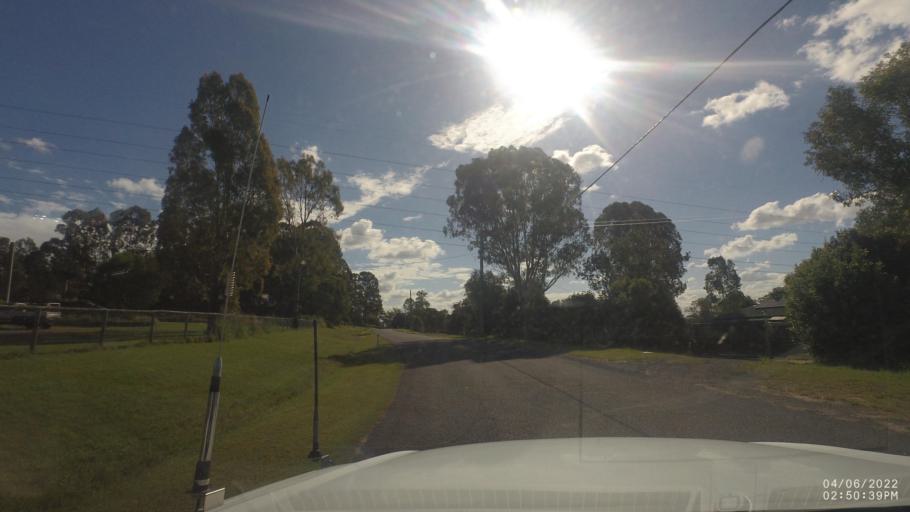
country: AU
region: Queensland
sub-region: Logan
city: Chambers Flat
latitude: -27.7718
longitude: 153.0809
